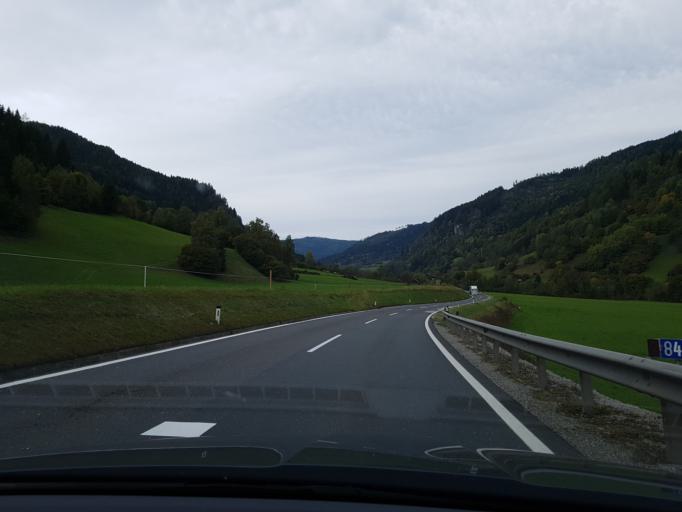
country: AT
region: Salzburg
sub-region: Politischer Bezirk Tamsweg
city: Ramingstein
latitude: 47.0688
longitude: 13.8771
